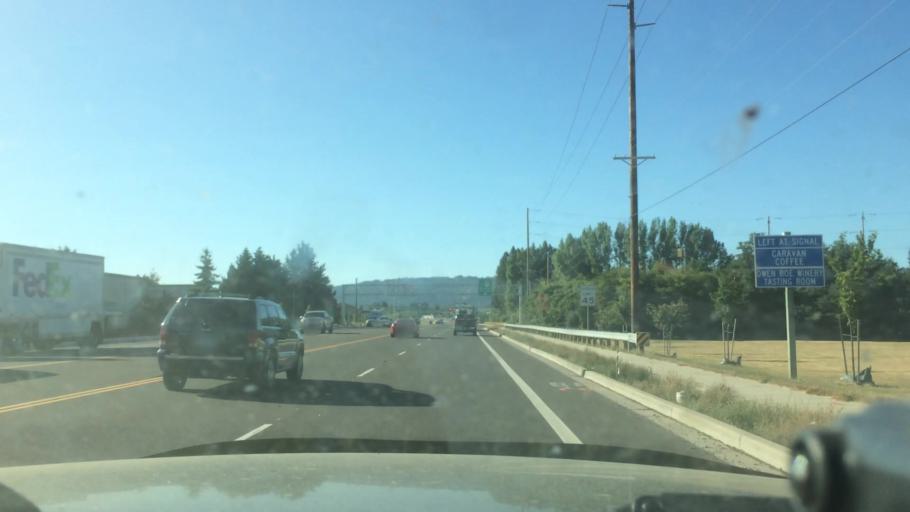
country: US
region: Oregon
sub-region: Yamhill County
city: Newberg
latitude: 45.2905
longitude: -122.9477
